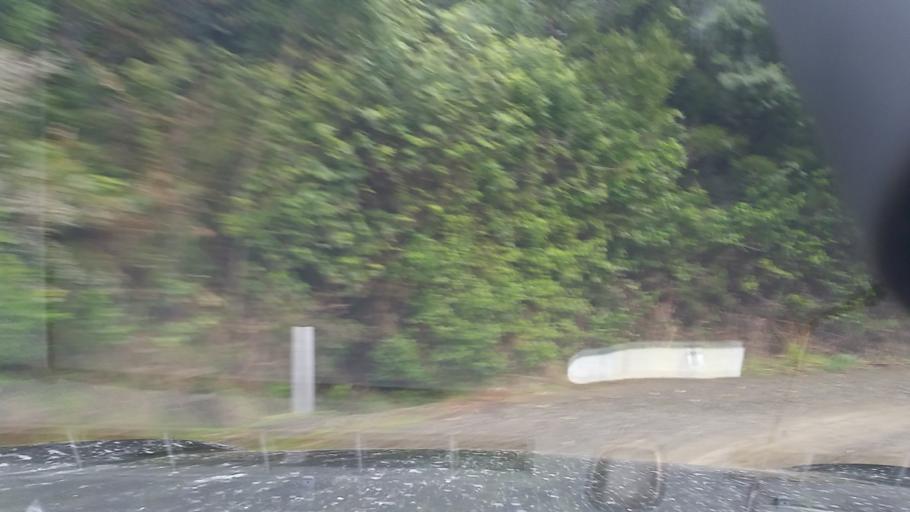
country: NZ
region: Nelson
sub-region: Nelson City
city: Nelson
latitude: -41.3618
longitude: 173.6111
